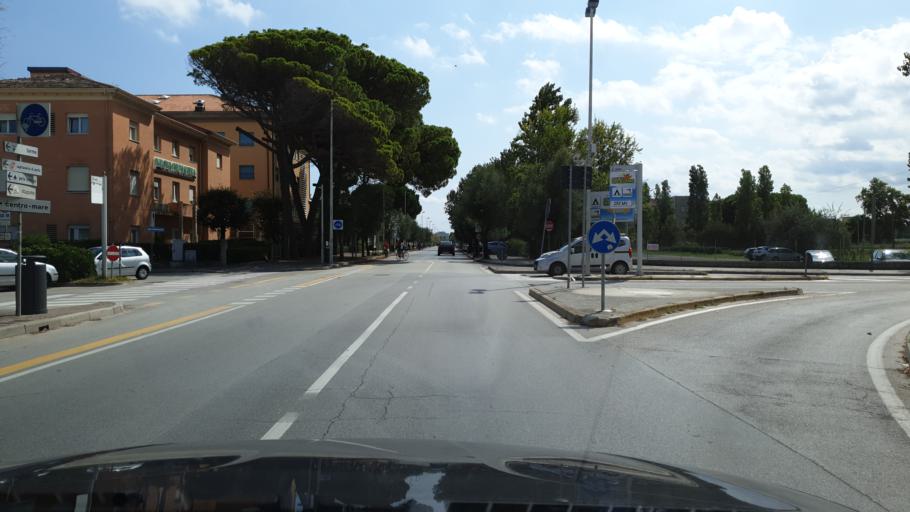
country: IT
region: Emilia-Romagna
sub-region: Provincia di Rimini
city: Misano Adriatico
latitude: 43.9890
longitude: 12.6827
